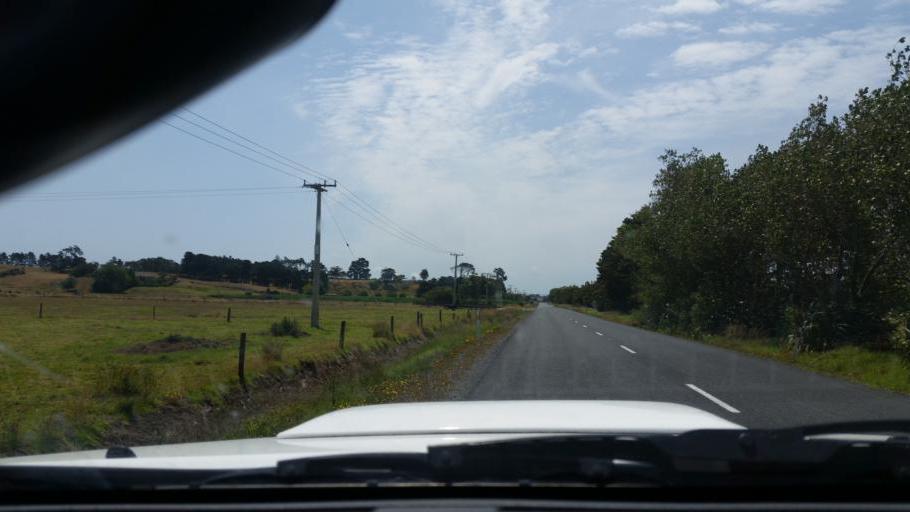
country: NZ
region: Northland
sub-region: Kaipara District
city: Dargaville
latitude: -36.0652
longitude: 173.9390
